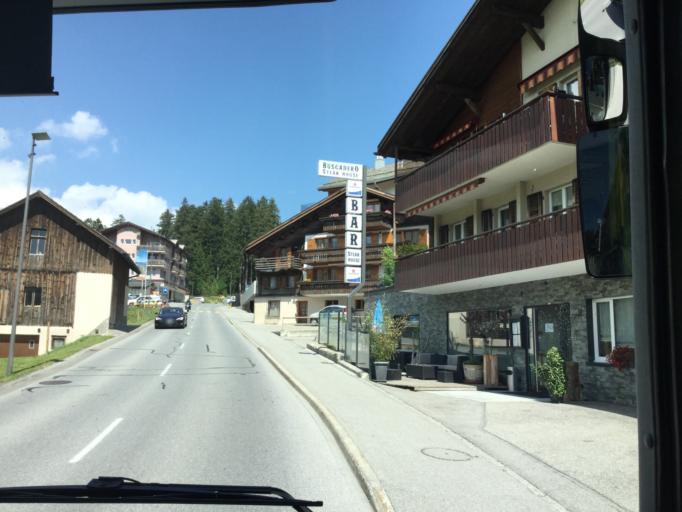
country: CH
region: Grisons
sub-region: Plessur District
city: Churwalden
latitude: 46.7453
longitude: 9.5564
